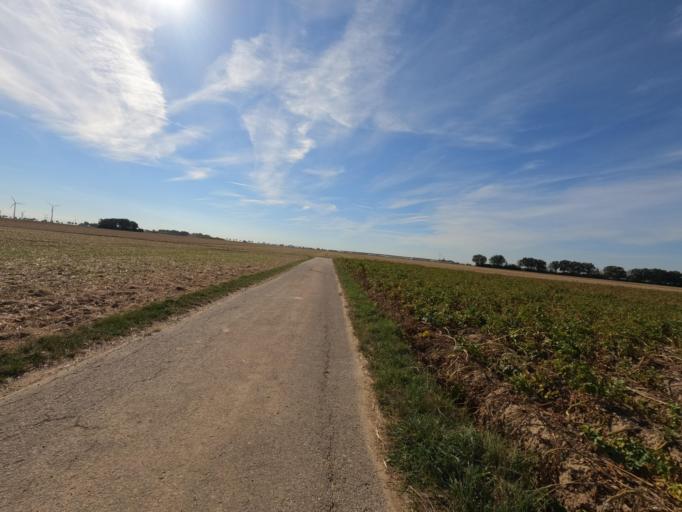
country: DE
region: North Rhine-Westphalia
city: Erkelenz
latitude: 51.0513
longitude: 6.3542
